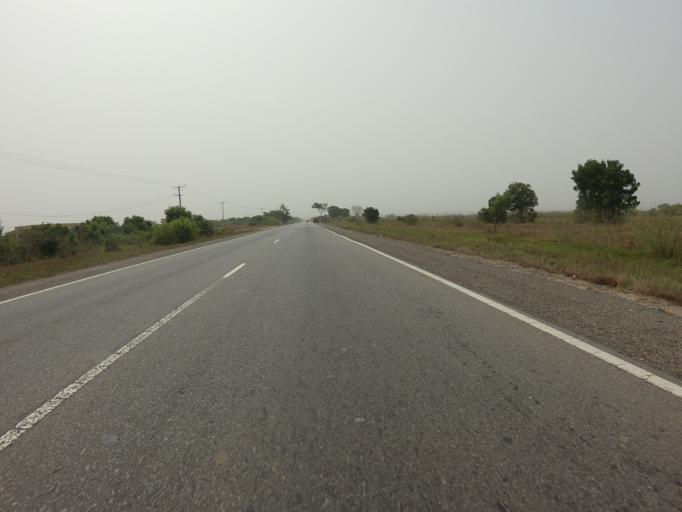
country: GH
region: Volta
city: Anloga
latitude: 5.9719
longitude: 0.5247
